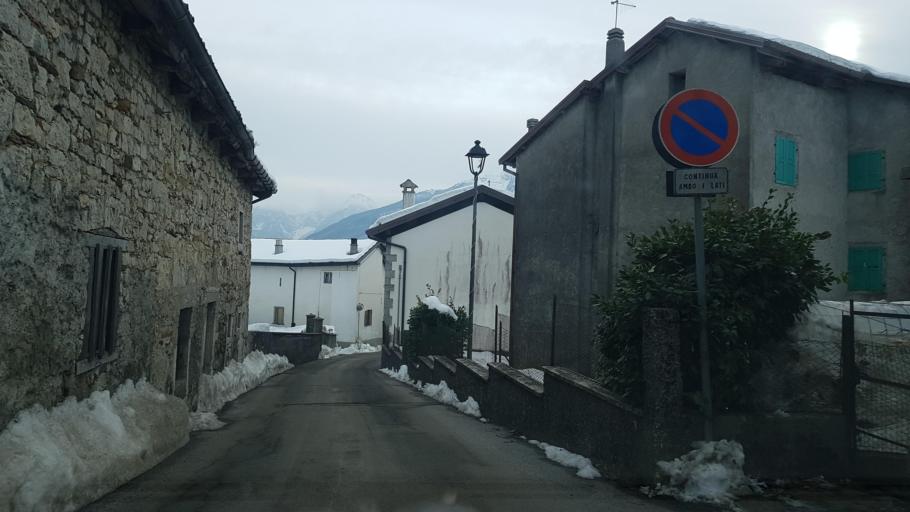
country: IT
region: Friuli Venezia Giulia
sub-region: Provincia di Udine
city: Lauco
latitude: 46.4250
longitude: 12.9323
